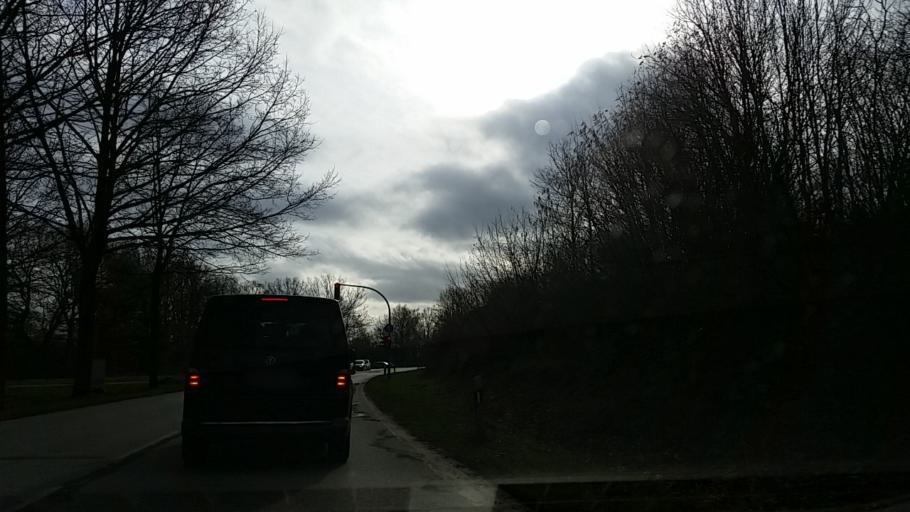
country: DE
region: Schleswig-Holstein
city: Bornsen
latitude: 53.4950
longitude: 10.2712
